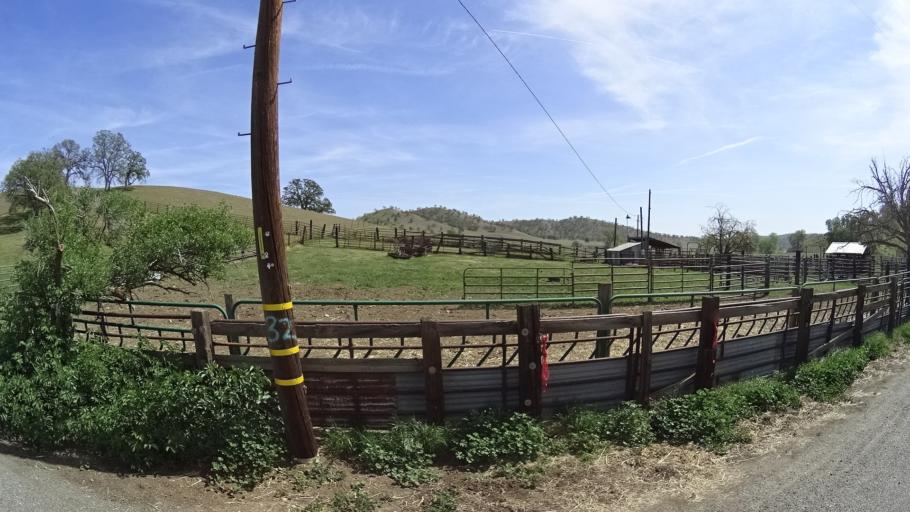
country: US
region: California
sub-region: Glenn County
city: Willows
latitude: 39.5561
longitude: -122.4384
